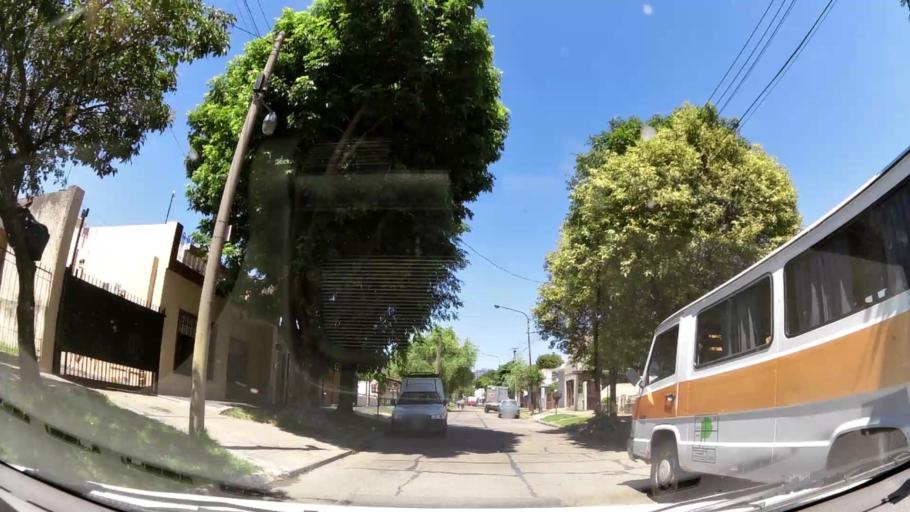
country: AR
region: Buenos Aires
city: Ituzaingo
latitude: -34.6735
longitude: -58.6871
